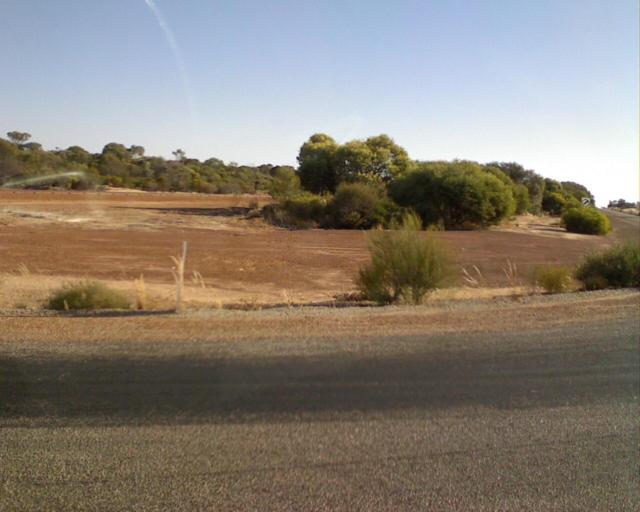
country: AU
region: Western Australia
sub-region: Wongan-Ballidu
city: Wongan Hills
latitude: -30.5208
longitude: 117.1773
